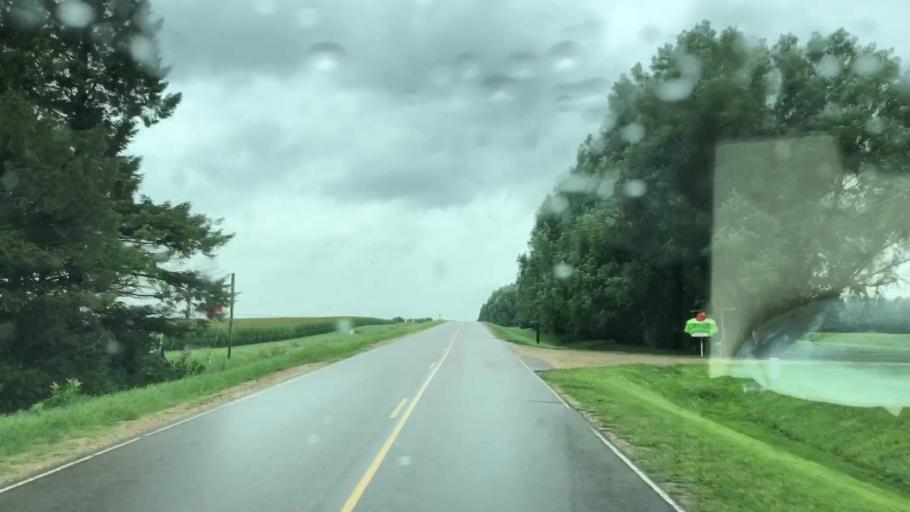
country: US
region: Iowa
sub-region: O'Brien County
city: Sanborn
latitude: 43.2375
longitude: -95.7235
